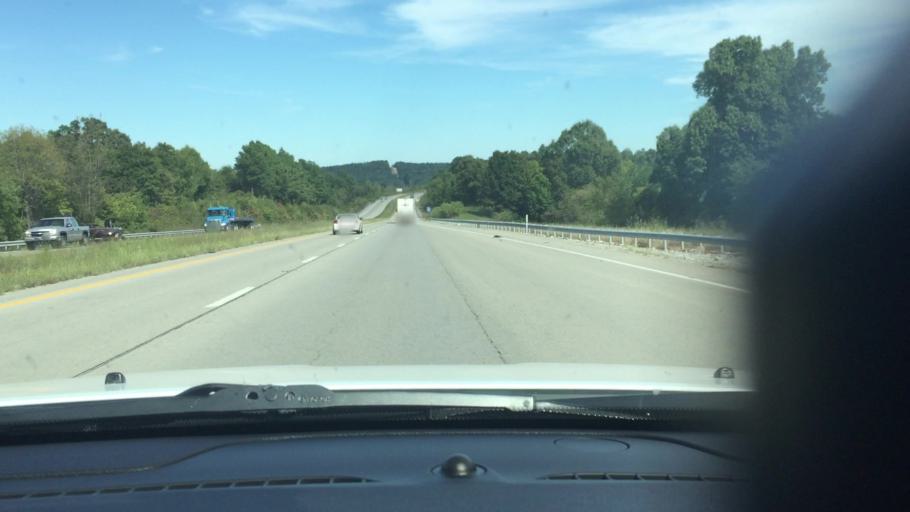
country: US
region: Kentucky
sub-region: Caldwell County
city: Princeton
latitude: 37.1349
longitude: -87.8646
